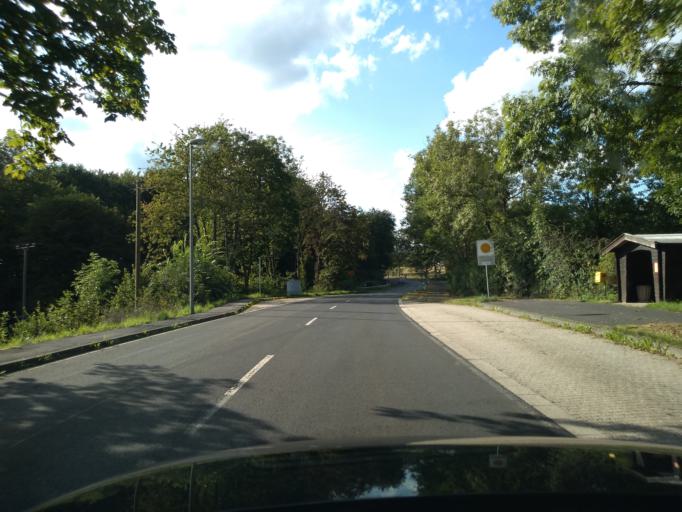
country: DE
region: North Rhine-Westphalia
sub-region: Regierungsbezirk Koln
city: Much
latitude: 50.8513
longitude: 7.3828
